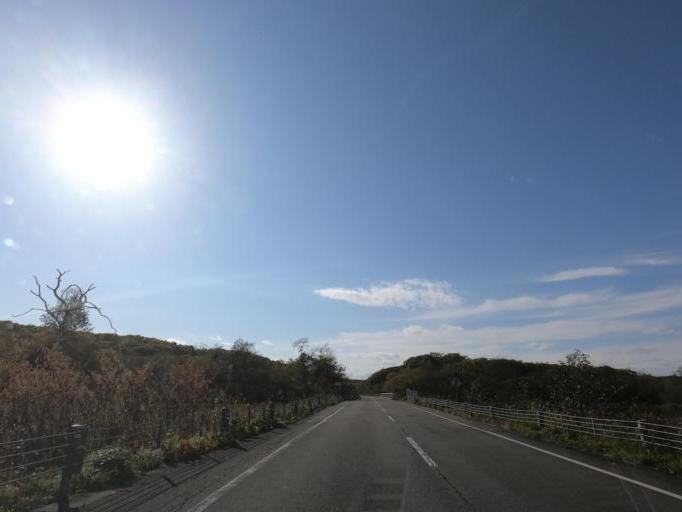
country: JP
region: Hokkaido
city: Obihiro
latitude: 42.6405
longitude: 143.5036
